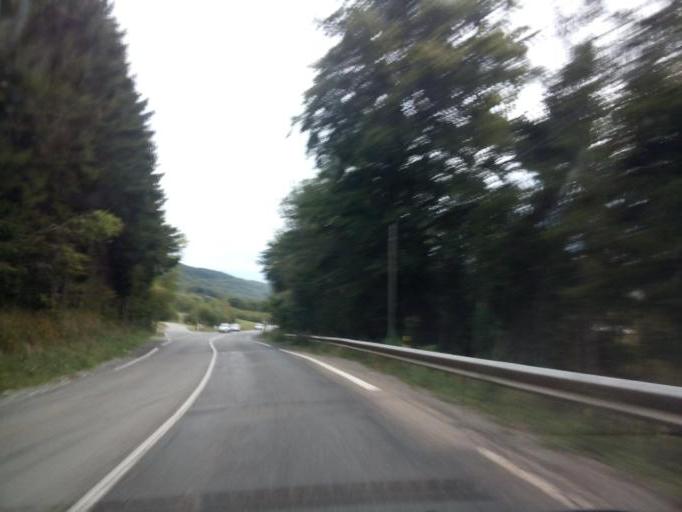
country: FR
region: Rhone-Alpes
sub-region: Departement de l'Isere
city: Pierre-Chatel
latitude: 44.9851
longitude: 5.7734
